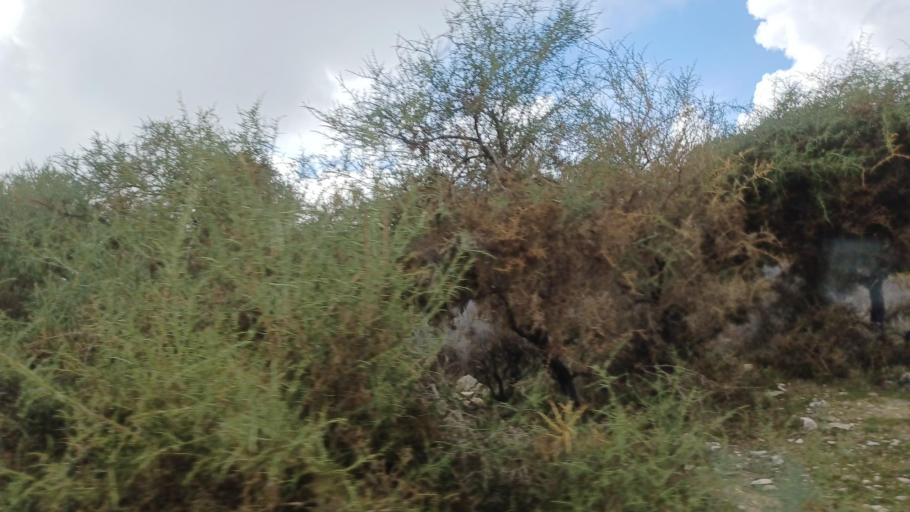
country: CY
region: Limassol
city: Sotira
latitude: 34.7267
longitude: 32.8237
